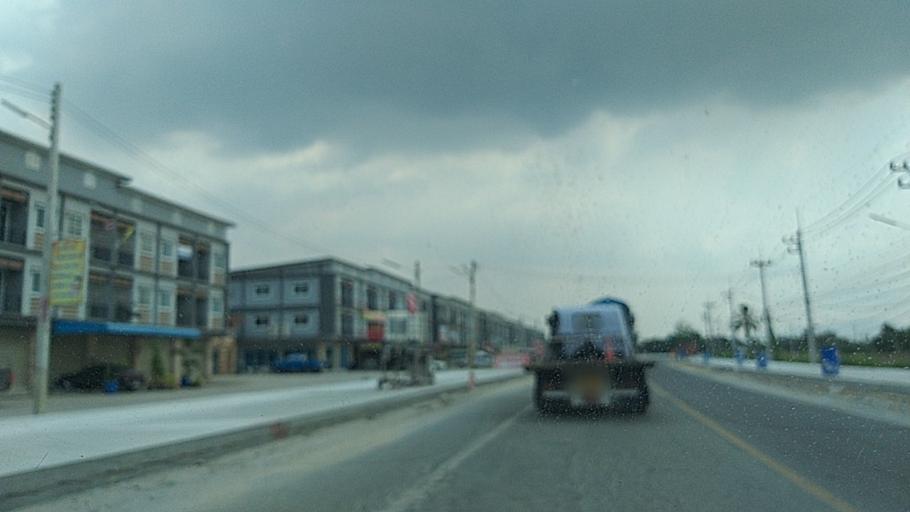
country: TH
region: Chon Buri
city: Ban Bueng
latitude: 13.3201
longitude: 101.1853
